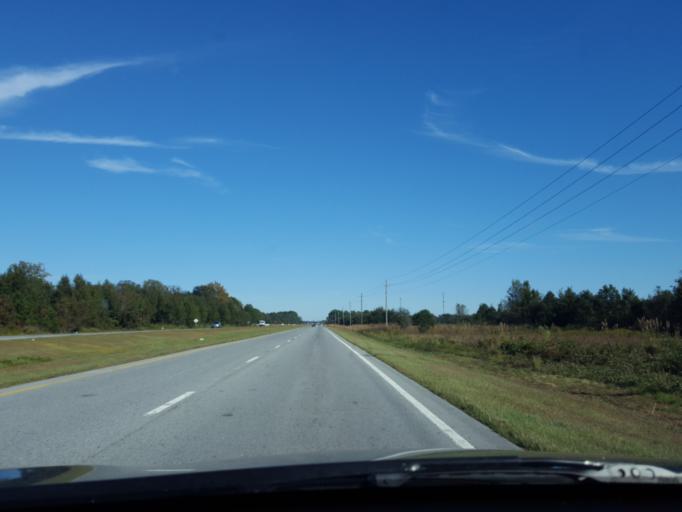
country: US
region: North Carolina
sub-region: Pitt County
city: Greenville
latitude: 35.6256
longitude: -77.2984
